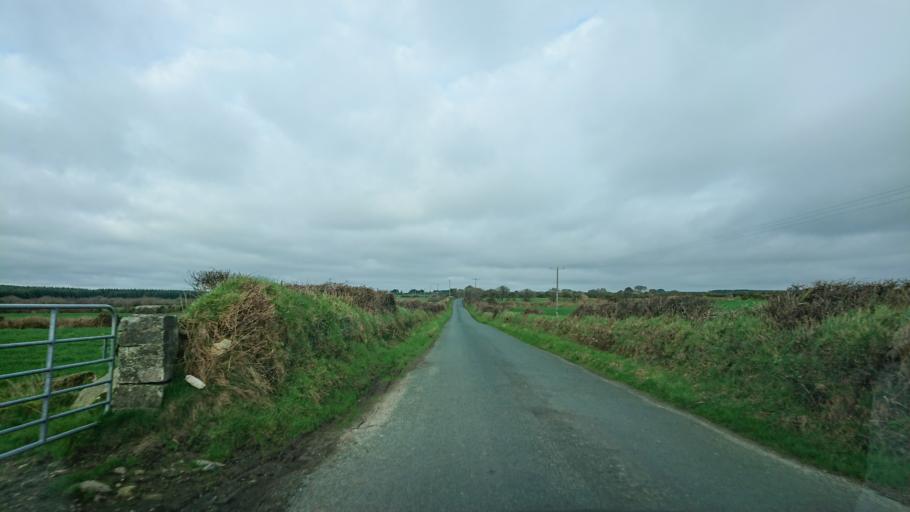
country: IE
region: Munster
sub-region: Waterford
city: Portlaw
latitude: 52.1541
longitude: -7.3094
